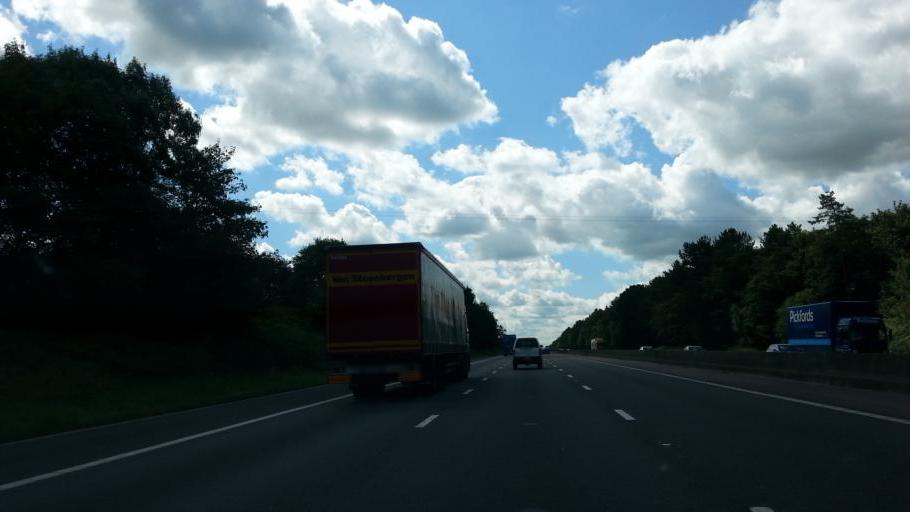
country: GB
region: England
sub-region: Leicestershire
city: Lutterworth
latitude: 52.4844
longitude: -1.1920
